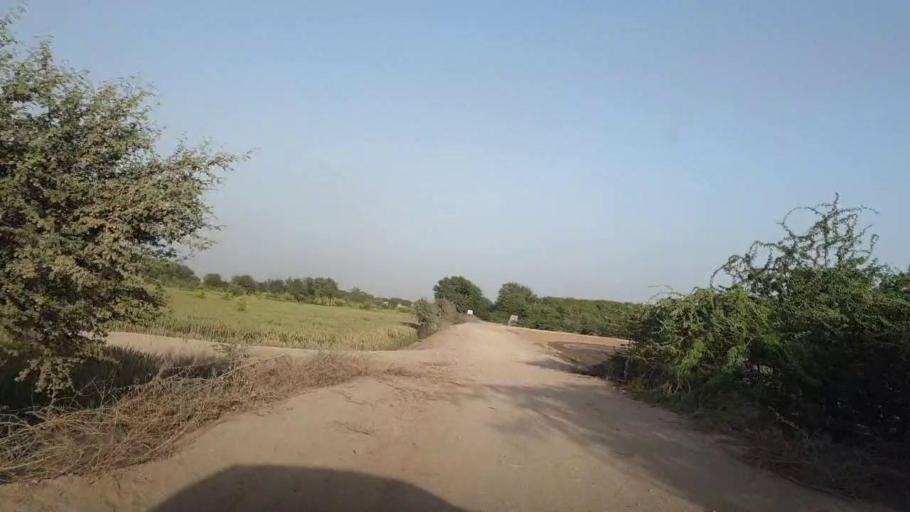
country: PK
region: Sindh
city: Tando Ghulam Ali
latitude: 25.1196
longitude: 68.9166
